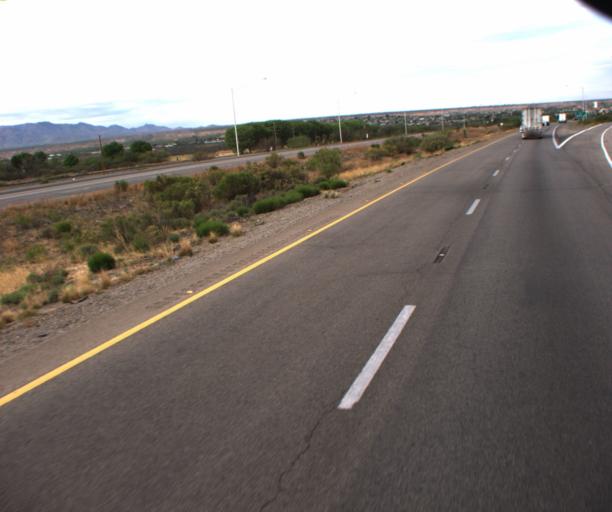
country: US
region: Arizona
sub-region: Cochise County
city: Benson
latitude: 31.9655
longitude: -110.2659
